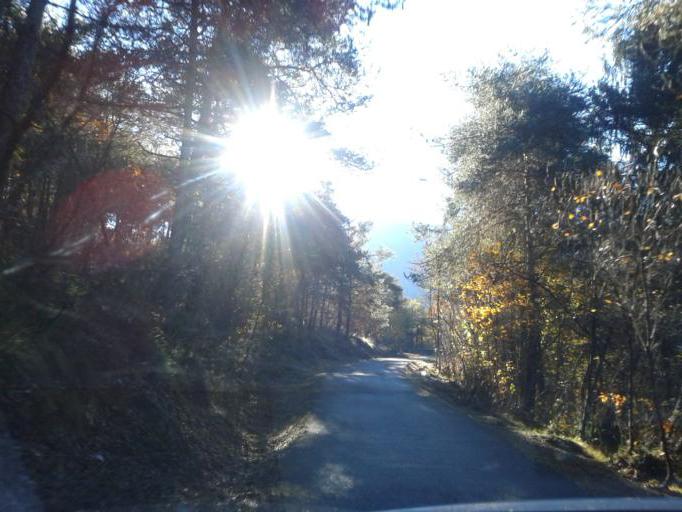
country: IT
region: Trentino-Alto Adige
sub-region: Provincia di Trento
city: Storo
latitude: 45.8469
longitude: 10.5922
